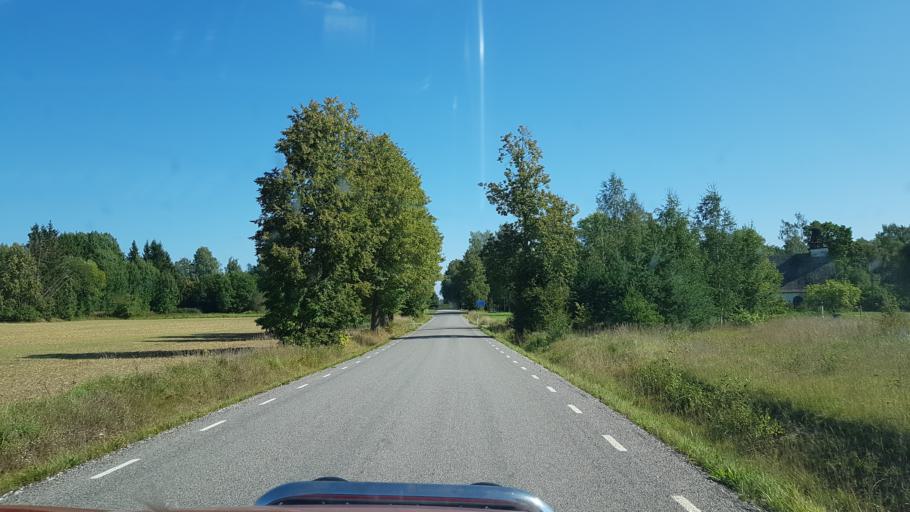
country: EE
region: Polvamaa
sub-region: Polva linn
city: Polva
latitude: 58.2097
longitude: 27.2522
